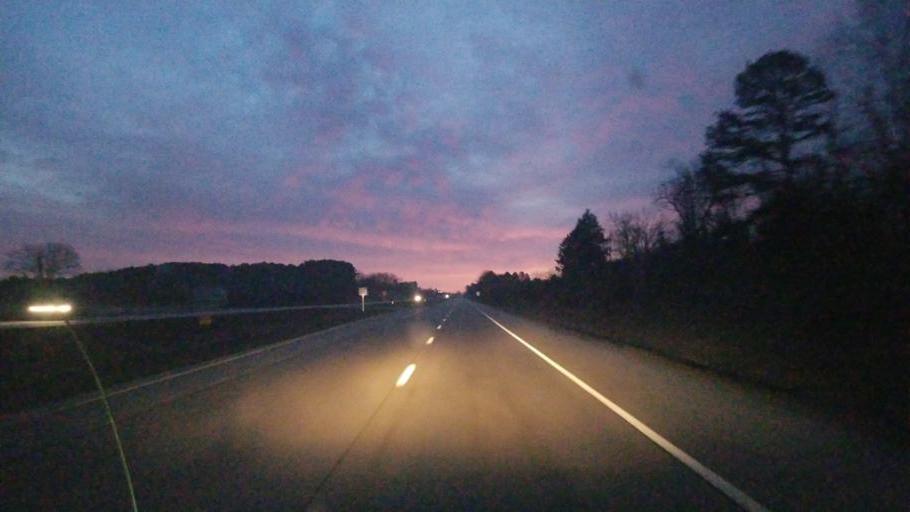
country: US
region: Missouri
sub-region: Shannon County
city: Winona
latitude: 36.9994
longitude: -91.4898
